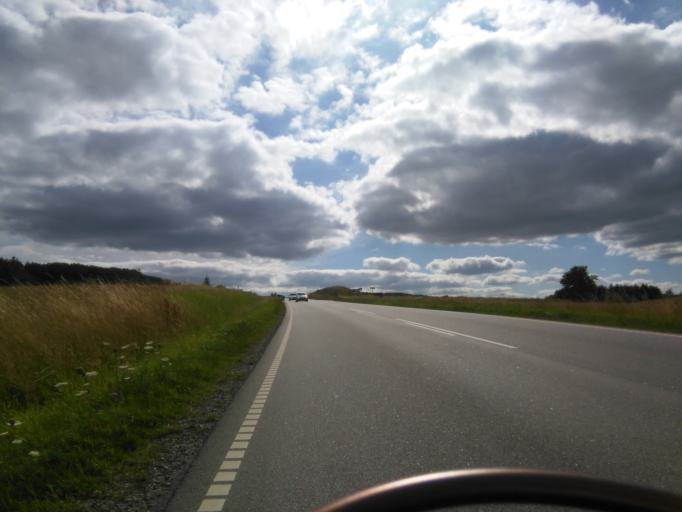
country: DK
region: Central Jutland
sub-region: Skanderborg Kommune
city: Stilling
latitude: 56.1098
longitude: 9.9785
